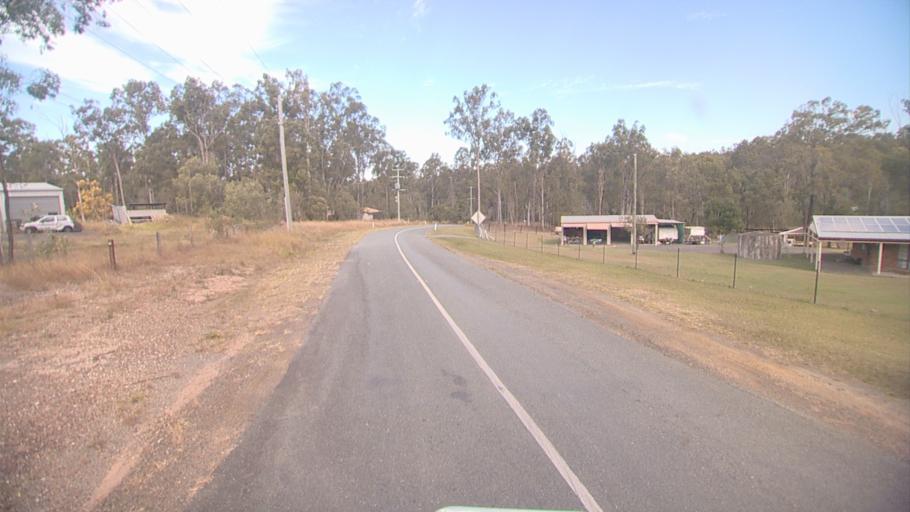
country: AU
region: Queensland
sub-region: Logan
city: North Maclean
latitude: -27.7379
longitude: 152.9792
